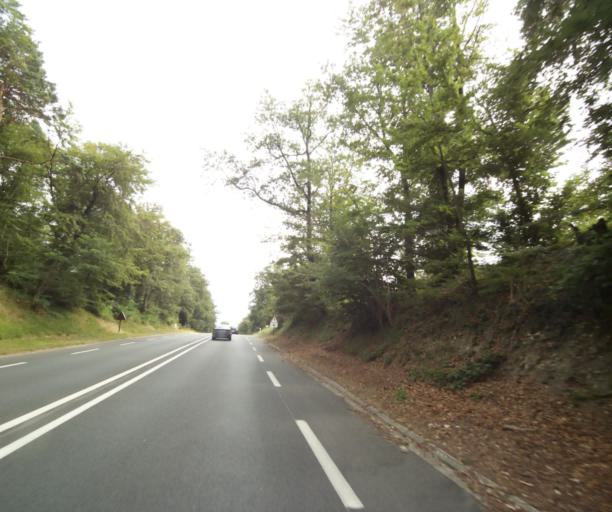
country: FR
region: Ile-de-France
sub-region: Departement de Seine-et-Marne
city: Fontainebleau
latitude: 48.4298
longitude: 2.7021
